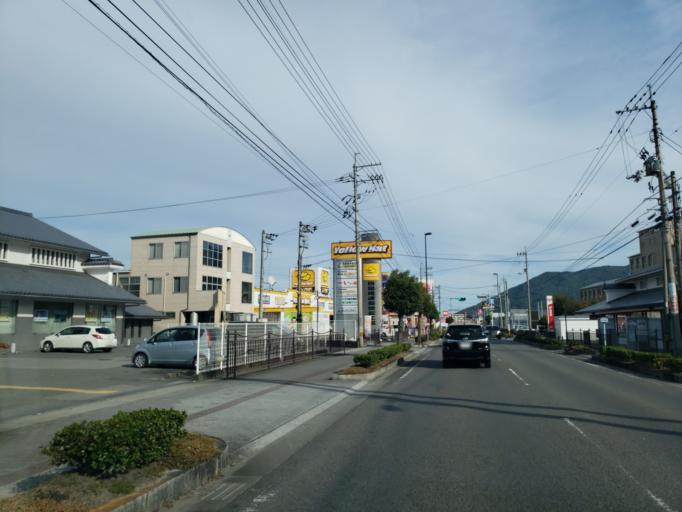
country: JP
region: Tokushima
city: Wakimachi
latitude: 34.0645
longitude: 134.1550
